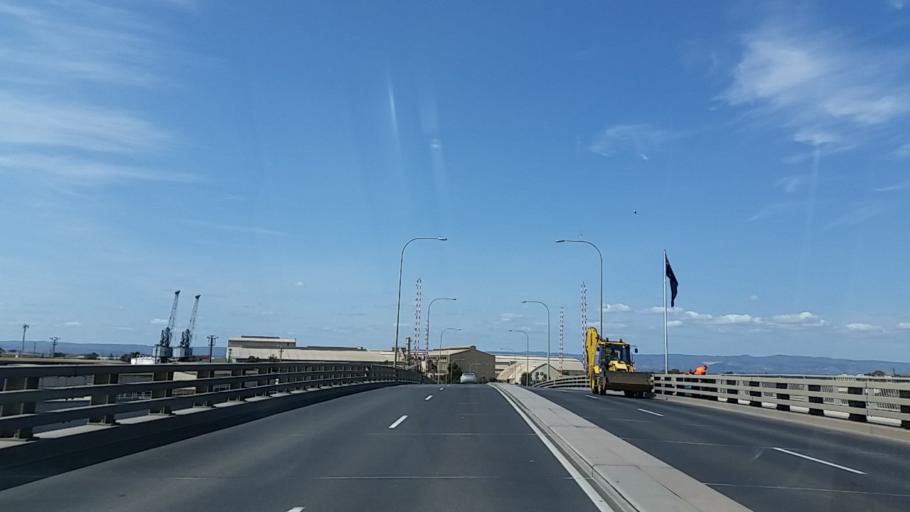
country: AU
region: South Australia
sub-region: Port Adelaide Enfield
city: Birkenhead
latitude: -34.8379
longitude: 138.5068
